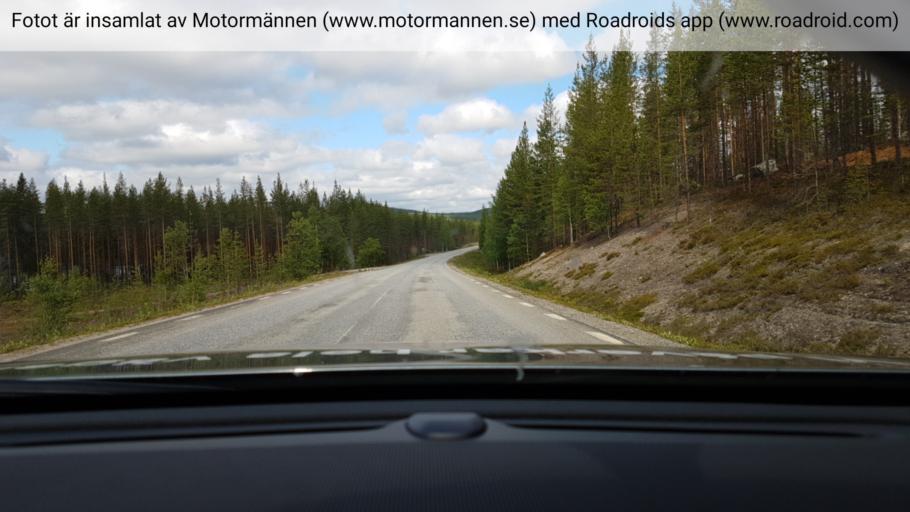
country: SE
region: Vaesterbotten
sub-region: Lycksele Kommun
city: Lycksele
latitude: 64.8561
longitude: 18.7358
